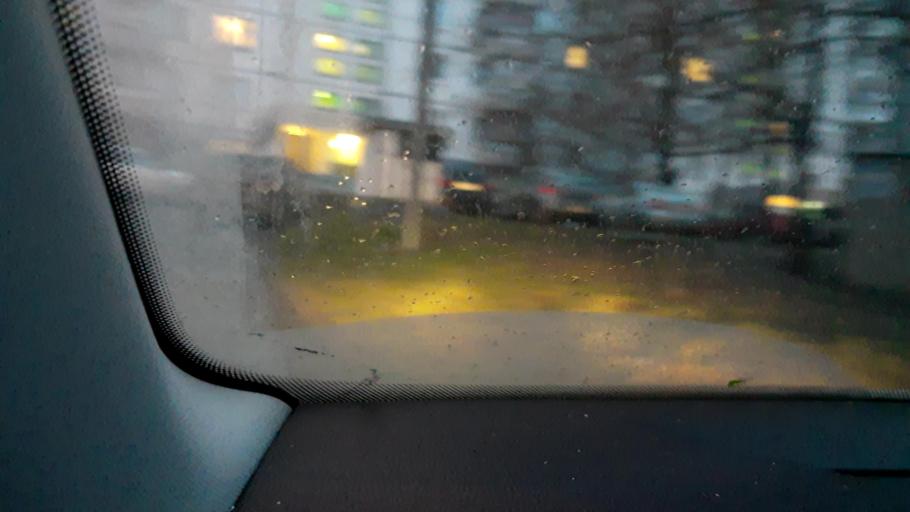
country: RU
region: Moscow
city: Orekhovo-Borisovo
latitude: 55.6200
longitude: 37.7417
